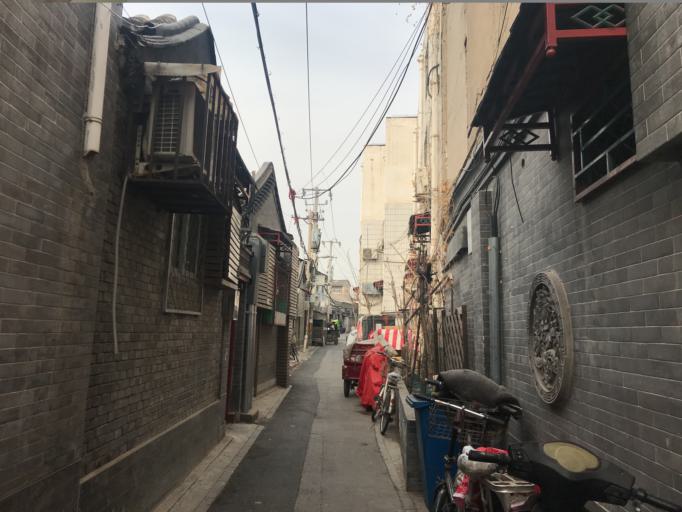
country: CN
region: Beijing
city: Beijing
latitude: 39.8890
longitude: 116.3852
